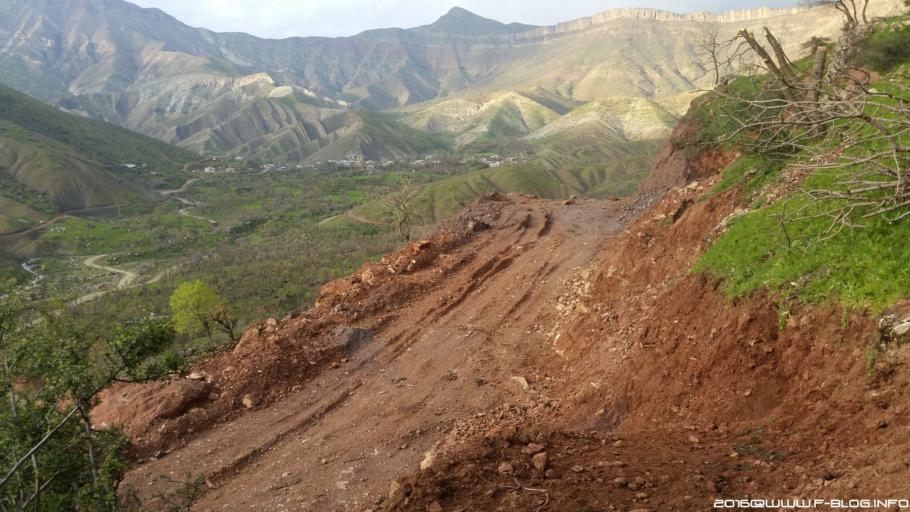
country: IQ
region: Arbil
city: Mergasur
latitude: 37.1003
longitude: 44.3217
